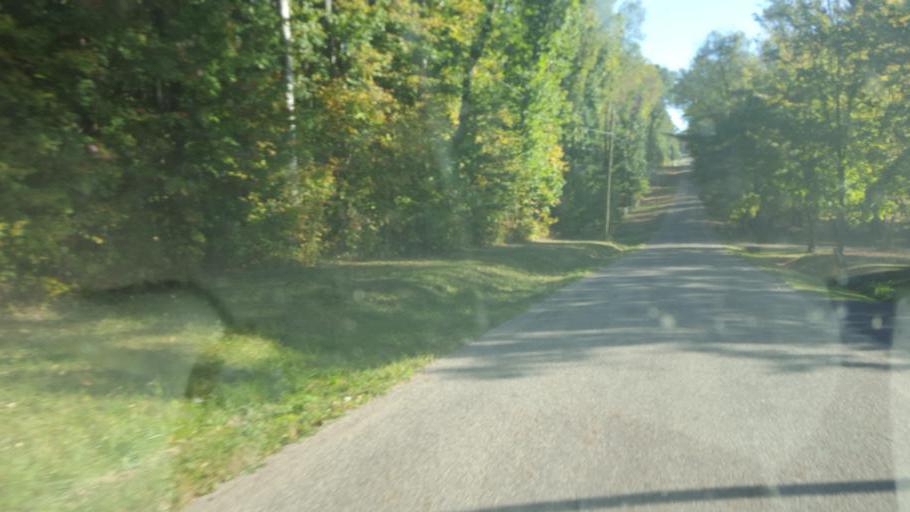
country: US
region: Ohio
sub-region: Richland County
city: Lexington
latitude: 40.6368
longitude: -82.5782
